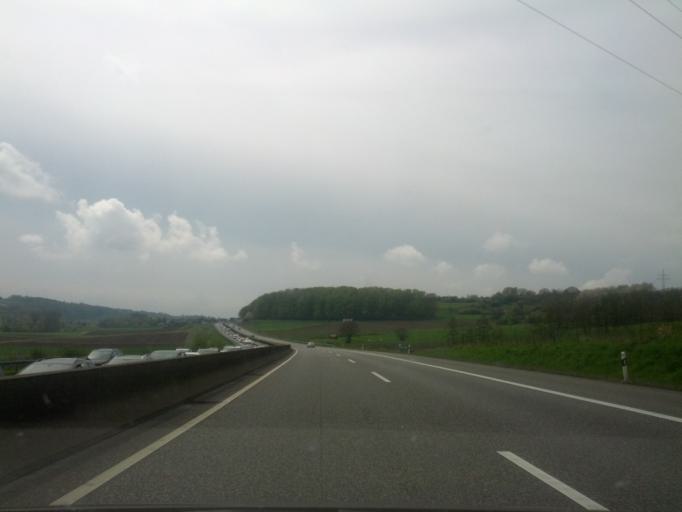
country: DE
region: Hesse
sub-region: Regierungsbezirk Giessen
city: Homberg
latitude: 50.6946
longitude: 9.0415
